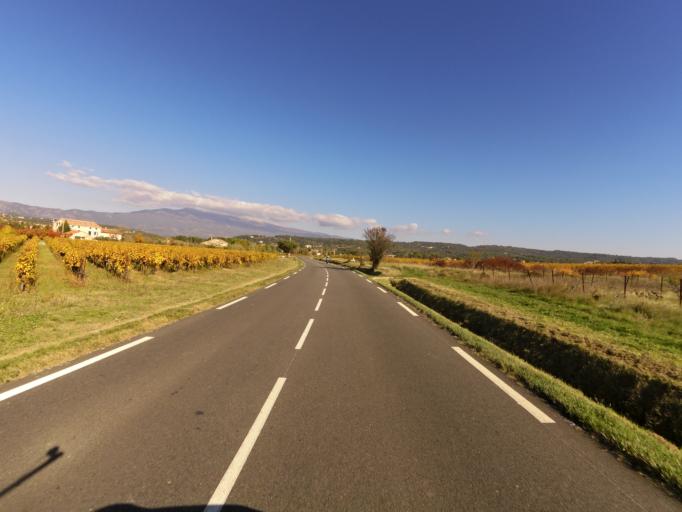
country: FR
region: Provence-Alpes-Cote d'Azur
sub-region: Departement du Vaucluse
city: Caromb
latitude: 44.0929
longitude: 5.1323
